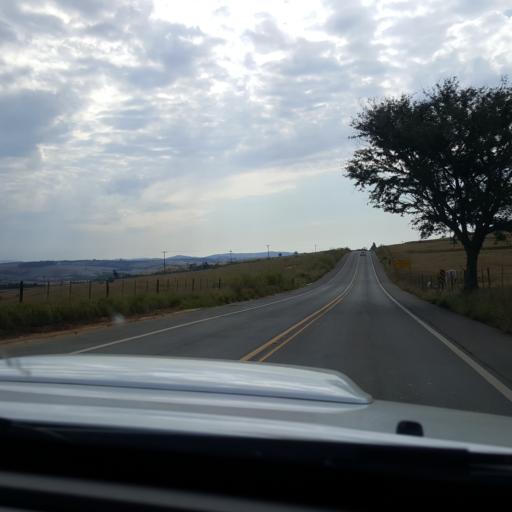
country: BR
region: Sao Paulo
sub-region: Itaporanga
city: Itaporanga
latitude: -23.7659
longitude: -49.4469
